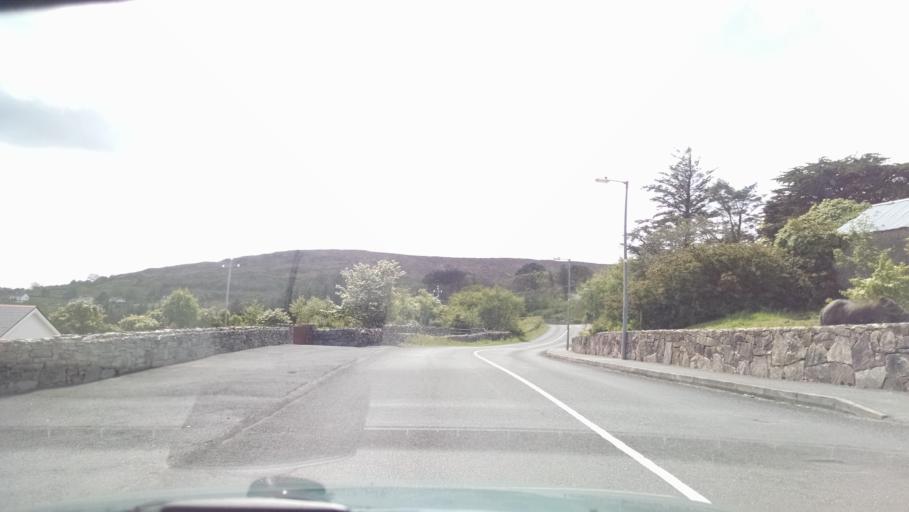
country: IE
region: Connaught
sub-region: County Galway
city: Clifden
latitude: 53.3267
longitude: -9.7341
